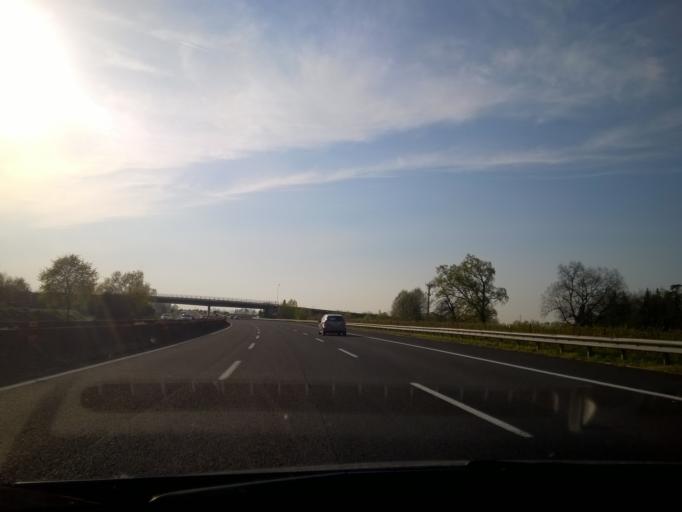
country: IT
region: Emilia-Romagna
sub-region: Provincia di Ravenna
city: Solarolo
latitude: 44.3382
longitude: 11.8681
